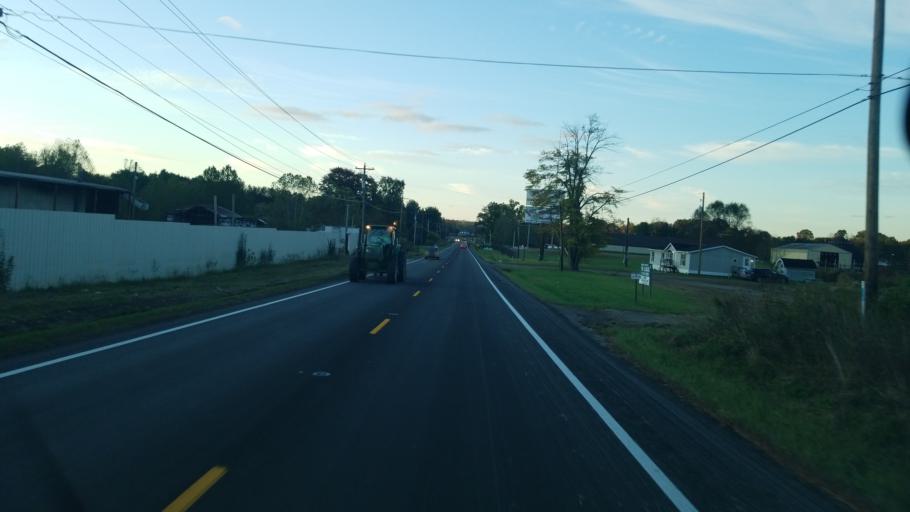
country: US
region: Ohio
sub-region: Vinton County
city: McArthur
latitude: 39.2126
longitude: -82.4820
